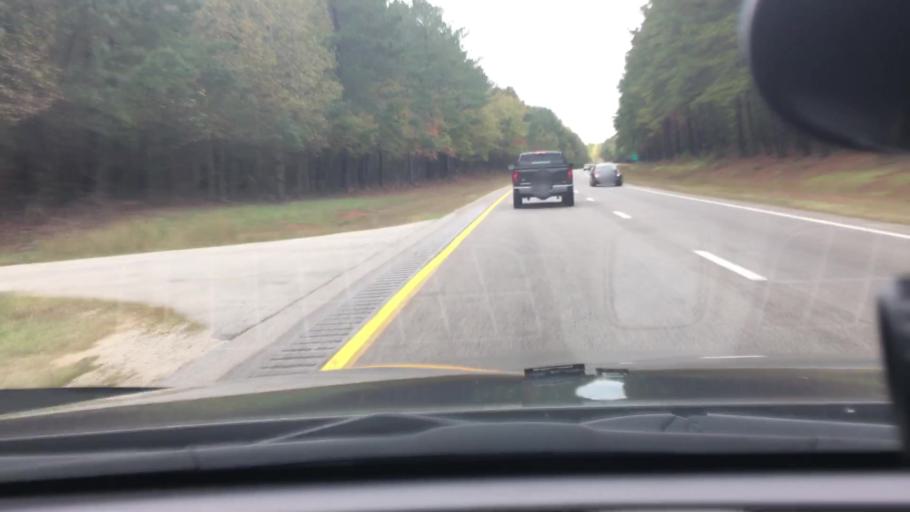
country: US
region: North Carolina
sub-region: Wake County
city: Zebulon
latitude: 35.7953
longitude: -78.1633
